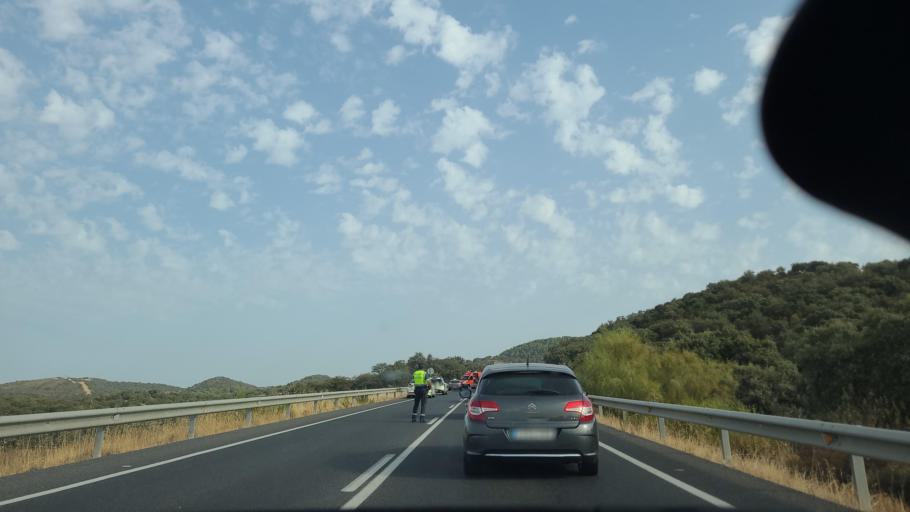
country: ES
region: Andalusia
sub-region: Province of Cordoba
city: Obejo
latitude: 38.0195
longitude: -4.8089
